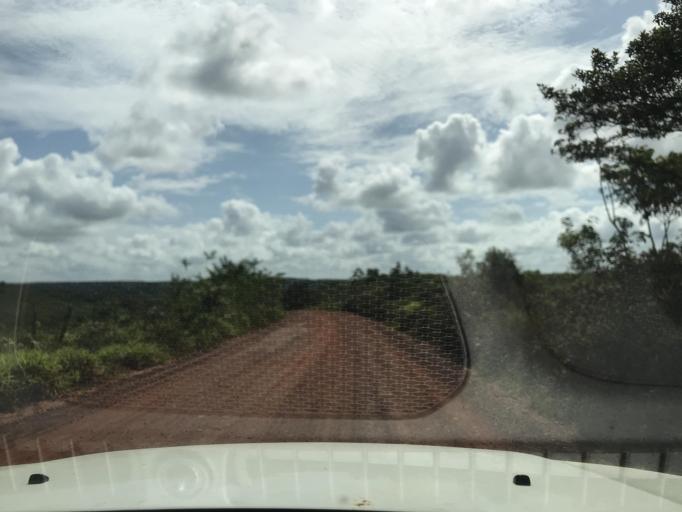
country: BR
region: Bahia
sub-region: Entre Rios
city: Entre Rios
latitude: -12.1706
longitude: -38.0983
